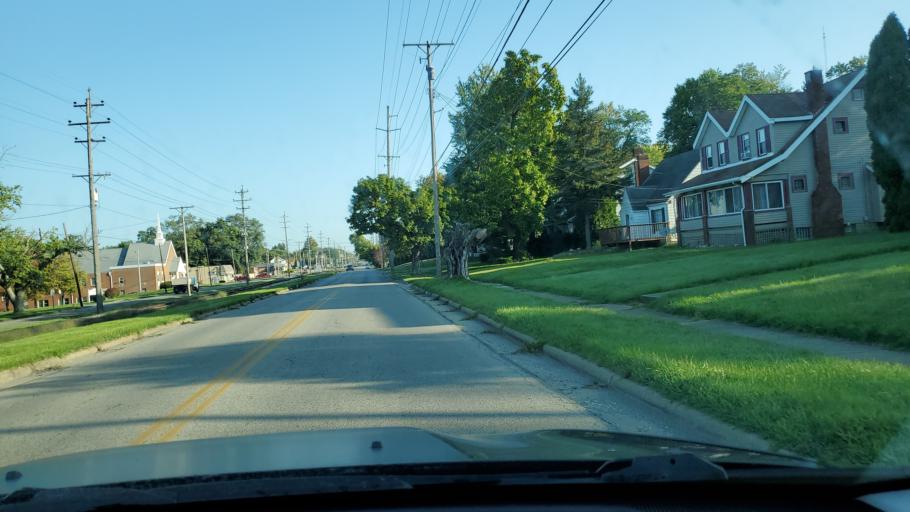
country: US
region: Ohio
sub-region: Mahoning County
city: Boardman
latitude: 41.0437
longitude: -80.6575
